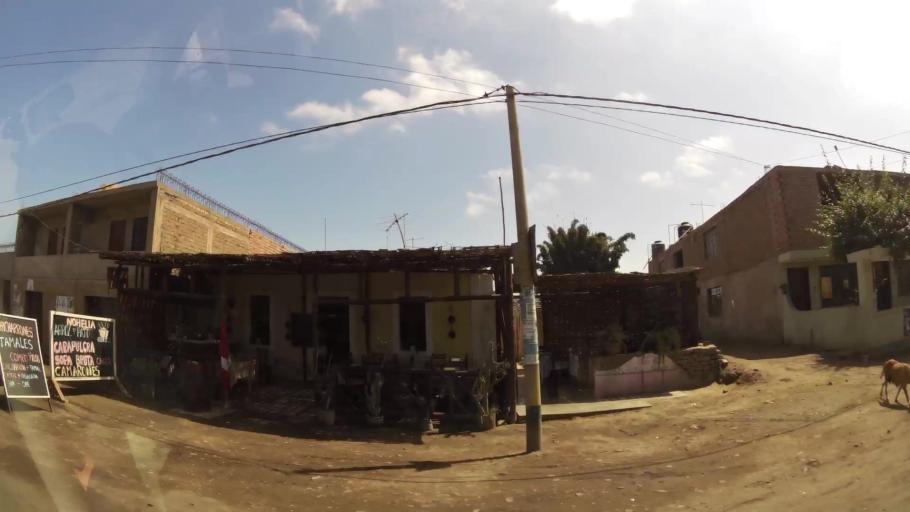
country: PE
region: Lima
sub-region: Provincia de Canete
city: Mala
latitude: -12.6644
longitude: -76.6404
